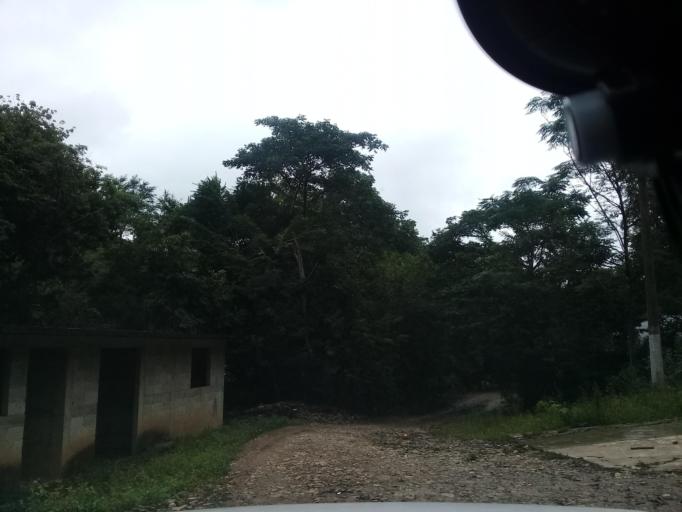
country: MX
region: Veracruz
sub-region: Chalma
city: San Pedro Coyutla
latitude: 21.2377
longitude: -98.4359
